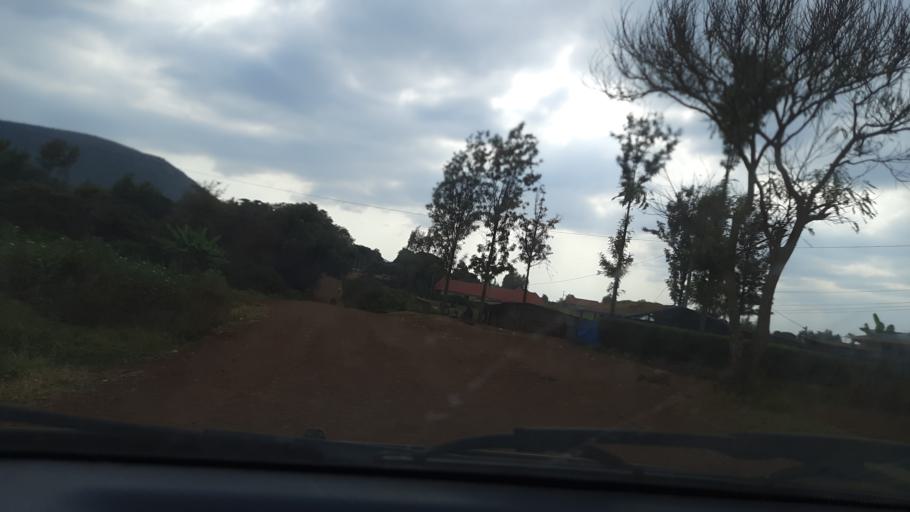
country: TZ
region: Arusha
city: Kingori
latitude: -2.8498
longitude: 37.2091
